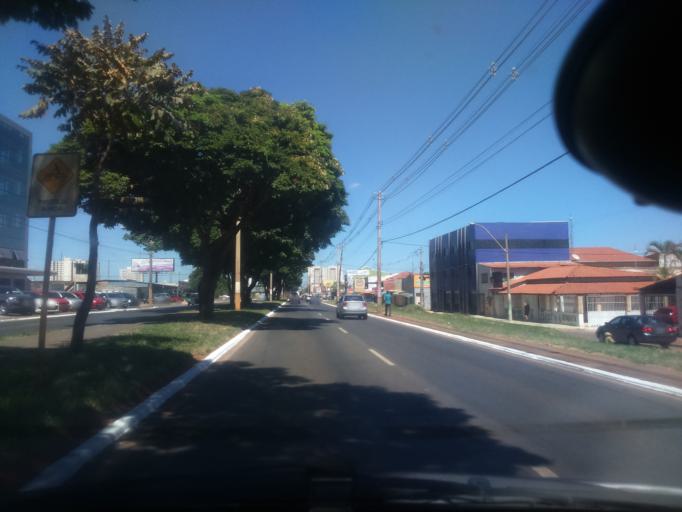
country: BR
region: Federal District
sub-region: Brasilia
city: Brasilia
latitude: -16.0007
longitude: -48.0595
